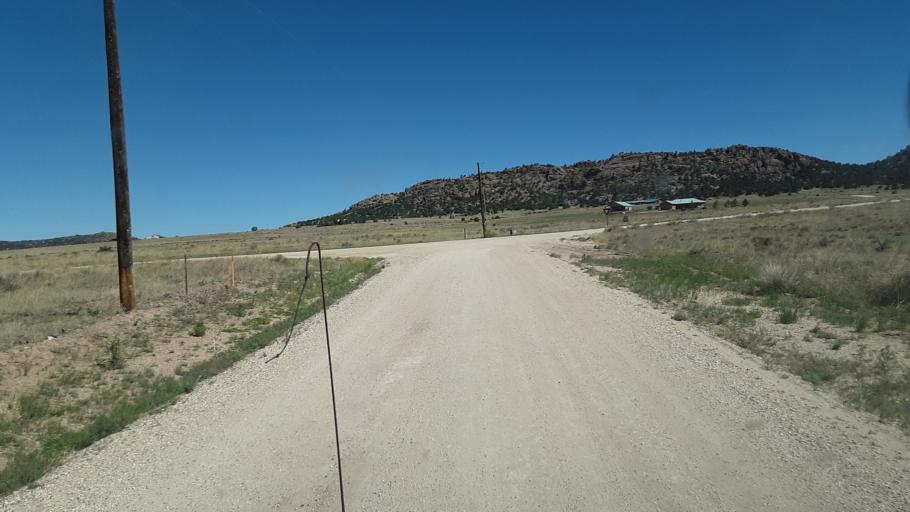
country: US
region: Colorado
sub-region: Custer County
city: Westcliffe
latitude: 38.2253
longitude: -105.4586
